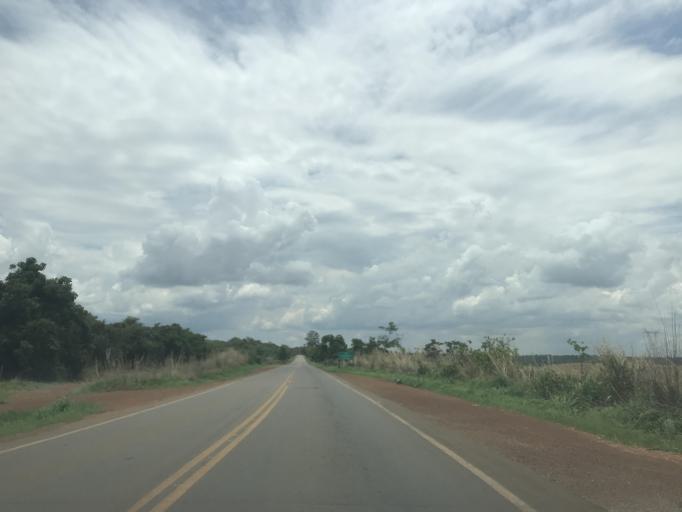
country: BR
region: Goias
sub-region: Vianopolis
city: Vianopolis
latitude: -16.7270
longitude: -48.4392
